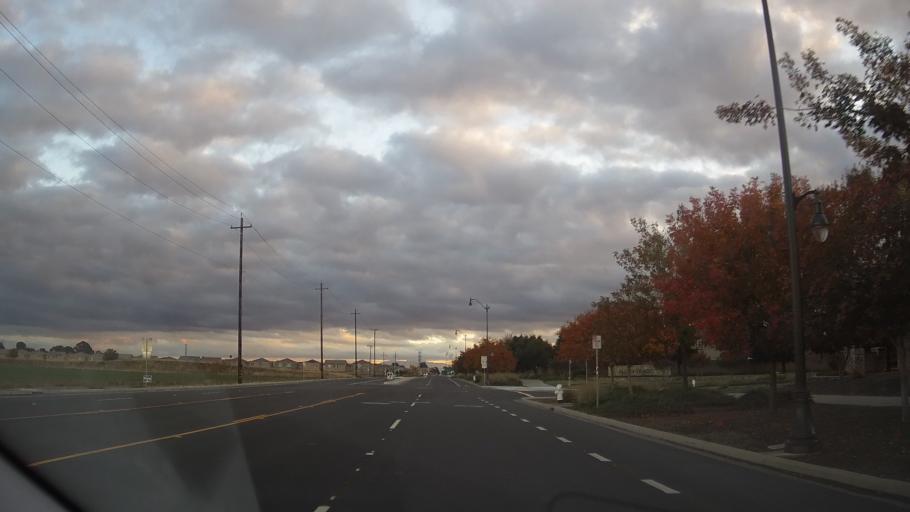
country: US
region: California
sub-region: Solano County
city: Vacaville
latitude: 38.3332
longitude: -121.9343
